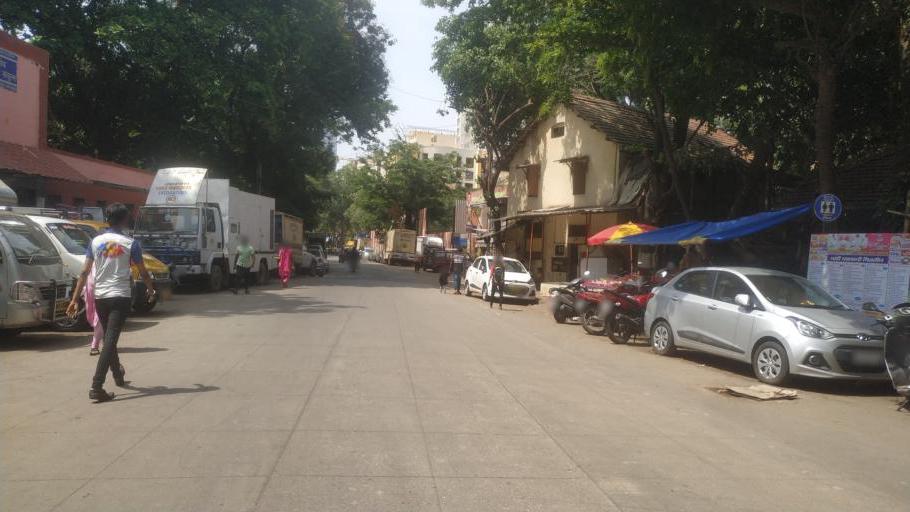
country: IN
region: Maharashtra
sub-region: Mumbai Suburban
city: Mumbai
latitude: 19.0006
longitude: 72.8463
